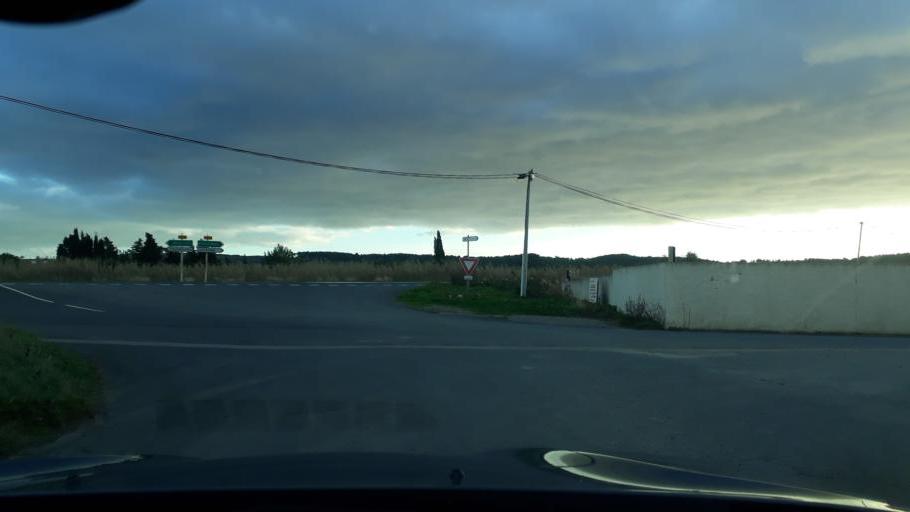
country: FR
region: Languedoc-Roussillon
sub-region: Departement de l'Herault
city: Nissan-lez-Enserune
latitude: 43.2911
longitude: 3.1180
